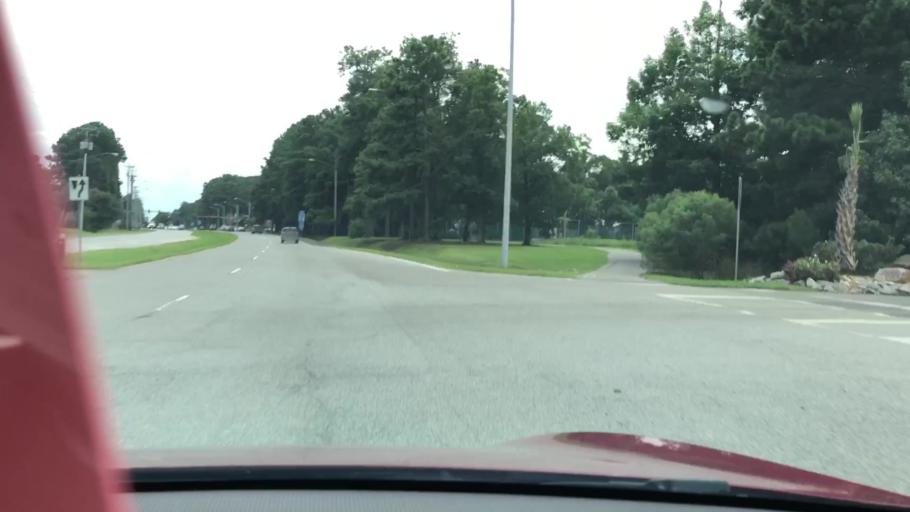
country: US
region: Virginia
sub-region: City of Virginia Beach
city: Virginia Beach
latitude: 36.8139
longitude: -75.9886
